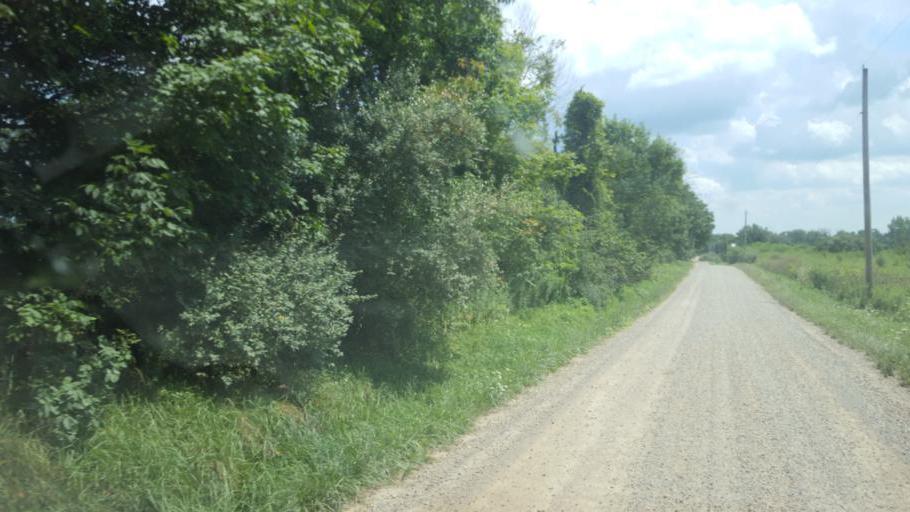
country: US
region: Ohio
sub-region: Knox County
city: Mount Vernon
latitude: 40.3639
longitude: -82.5838
